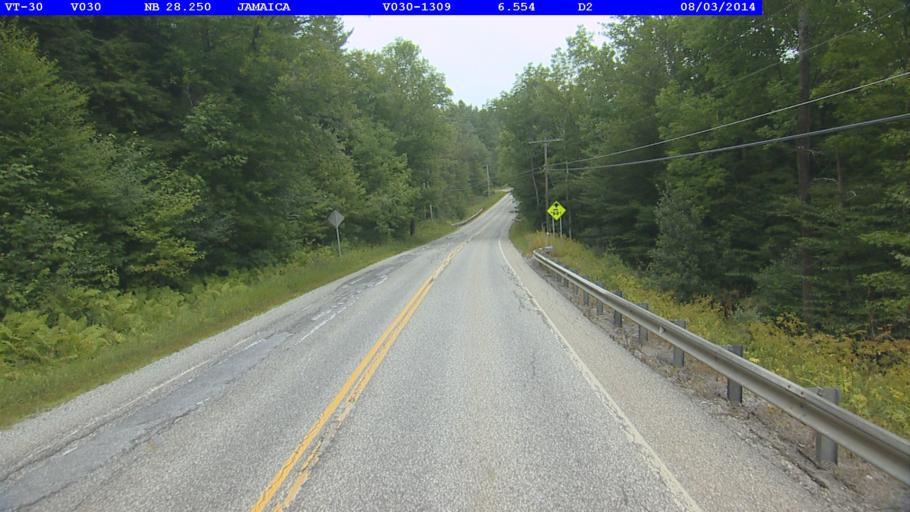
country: US
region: Vermont
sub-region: Windham County
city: Dover
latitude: 43.1248
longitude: -72.8120
